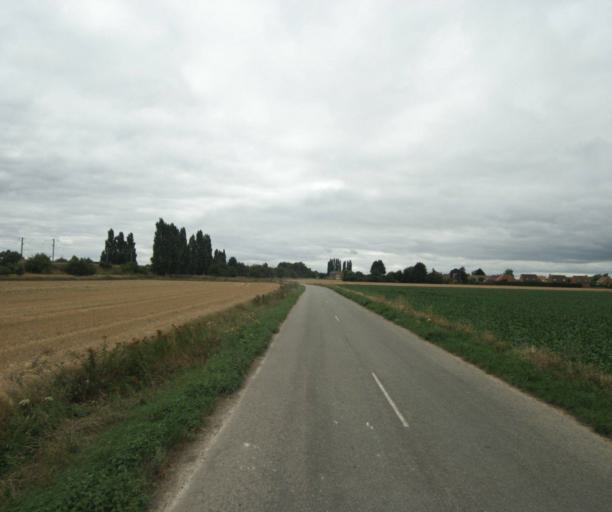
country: FR
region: Nord-Pas-de-Calais
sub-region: Departement du Nord
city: Avelin
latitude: 50.5511
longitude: 3.1043
